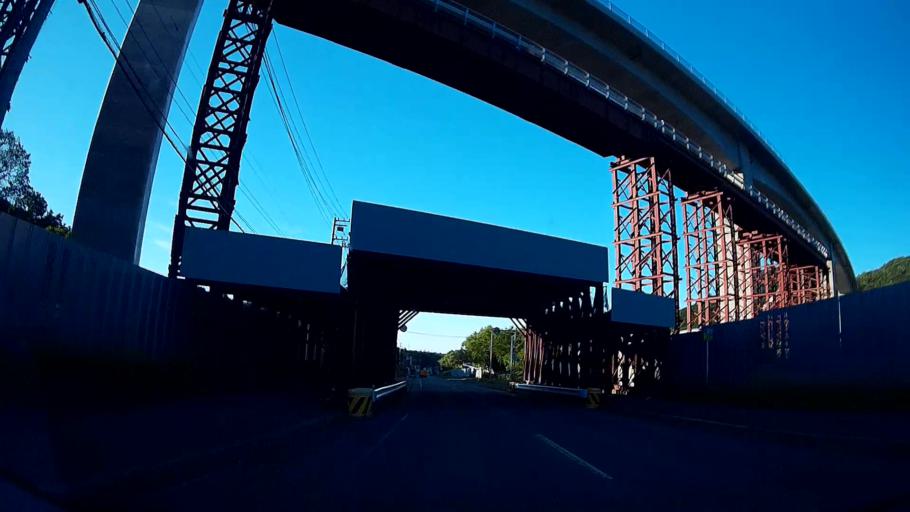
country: JP
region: Hokkaido
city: Otaru
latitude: 43.1524
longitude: 141.0413
